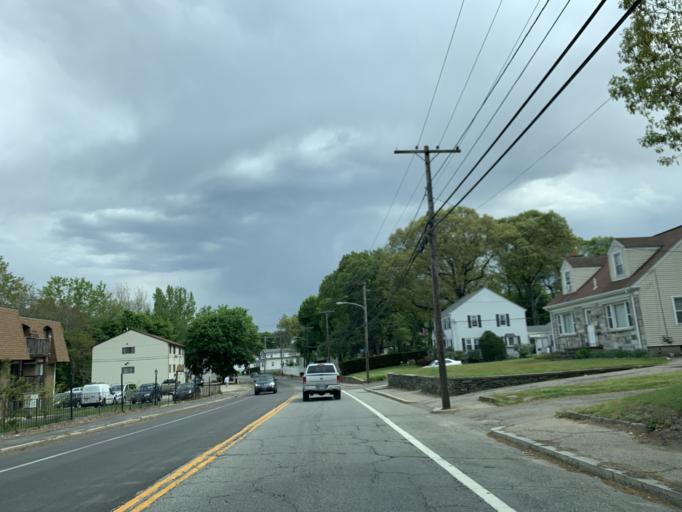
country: US
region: Rhode Island
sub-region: Providence County
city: Johnston
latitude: 41.7997
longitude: -71.4860
